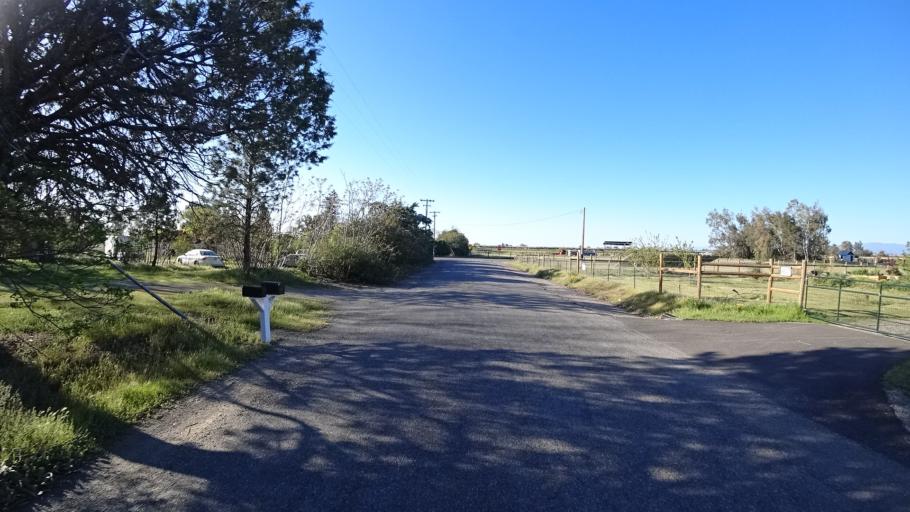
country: US
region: California
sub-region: Glenn County
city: Orland
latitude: 39.7556
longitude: -122.2298
